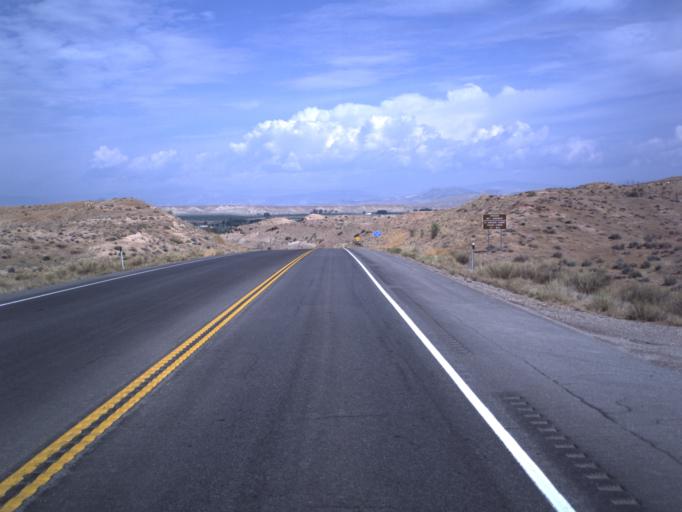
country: US
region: Utah
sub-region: Uintah County
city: Naples
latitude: 40.3658
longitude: -109.3229
